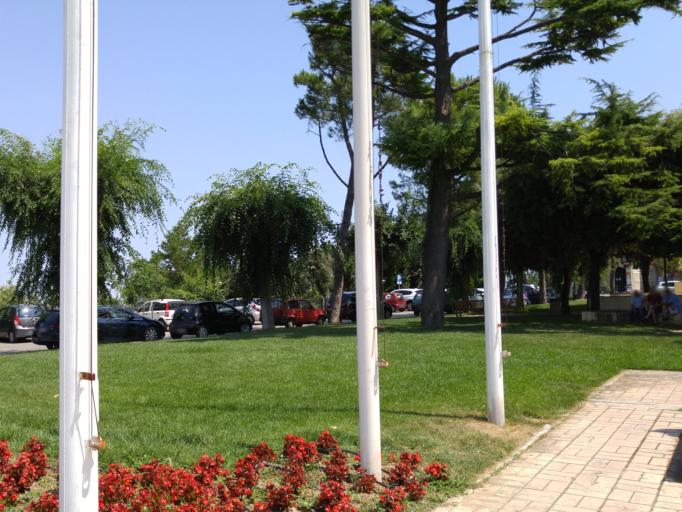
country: IT
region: Abruzzo
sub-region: Provincia di Pescara
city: Citta Sant'Angelo
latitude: 42.5198
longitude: 14.0624
